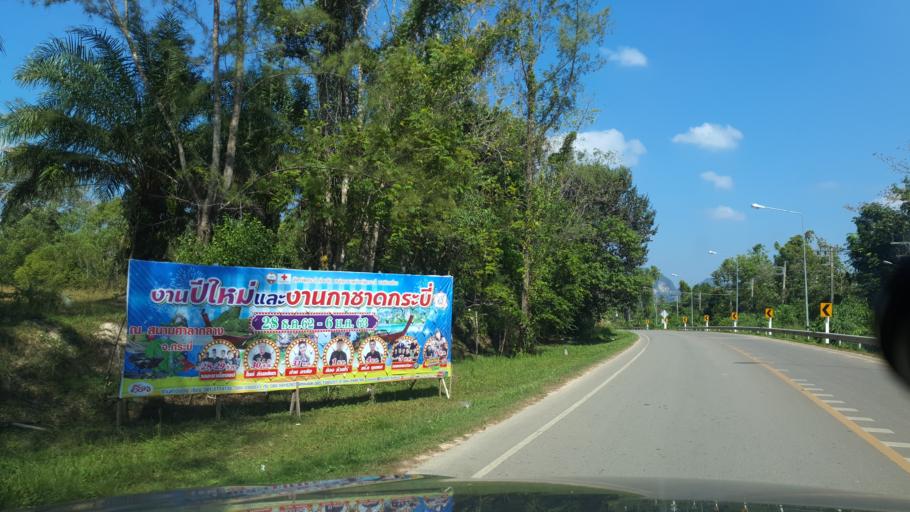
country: TH
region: Phangnga
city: Ban Ao Nang
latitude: 8.0431
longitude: 98.8613
